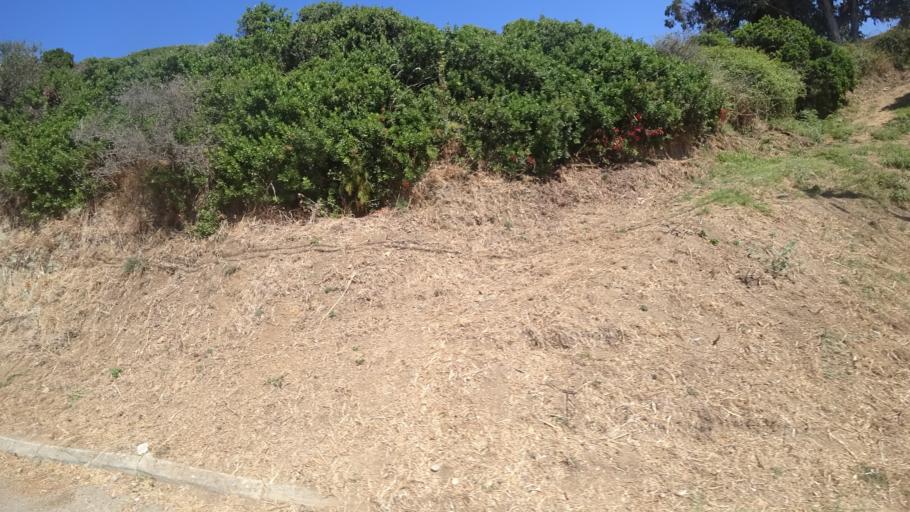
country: FR
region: Corsica
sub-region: Departement de la Corse-du-Sud
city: Alata
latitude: 41.9787
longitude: 8.6694
